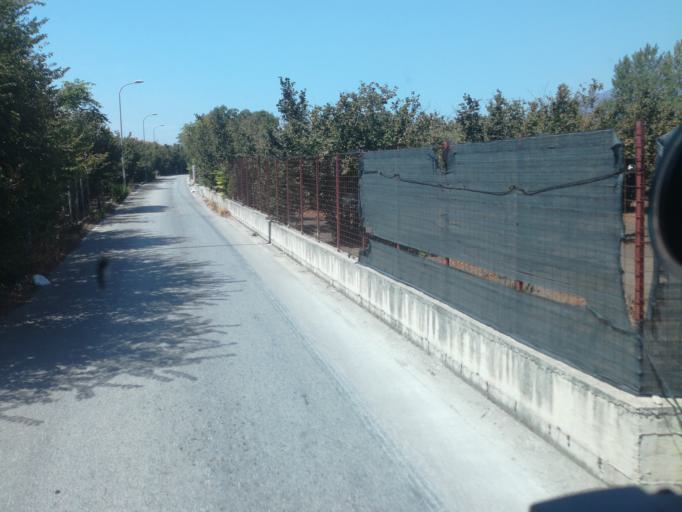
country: IT
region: Campania
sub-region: Provincia di Napoli
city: Poggiomarino
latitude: 40.7963
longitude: 14.5173
